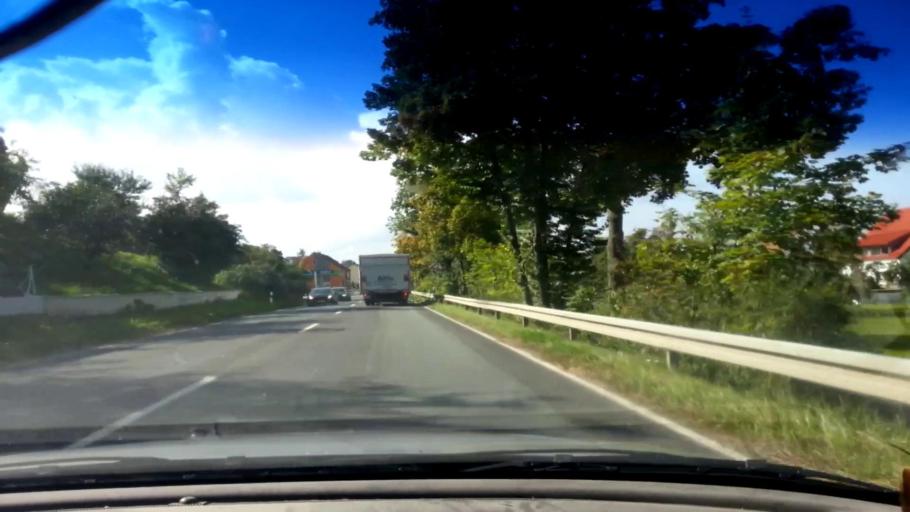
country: DE
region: Bavaria
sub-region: Upper Franconia
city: Viereth-Trunstadt
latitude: 49.9230
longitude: 10.7831
